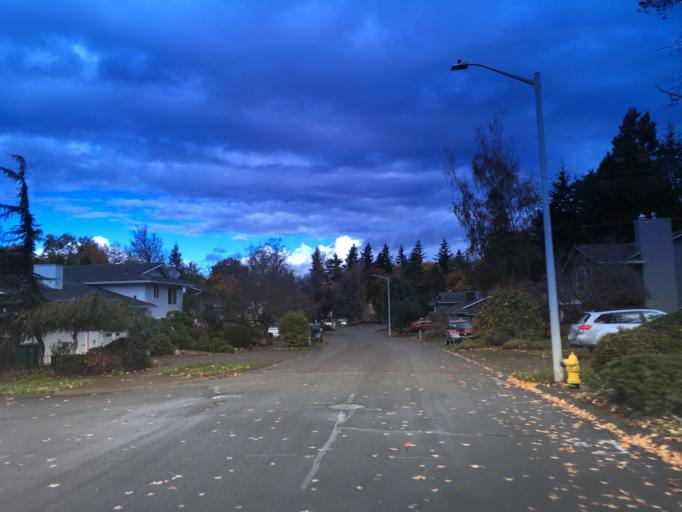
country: US
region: Oregon
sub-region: Multnomah County
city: Troutdale
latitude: 45.5165
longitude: -122.3767
